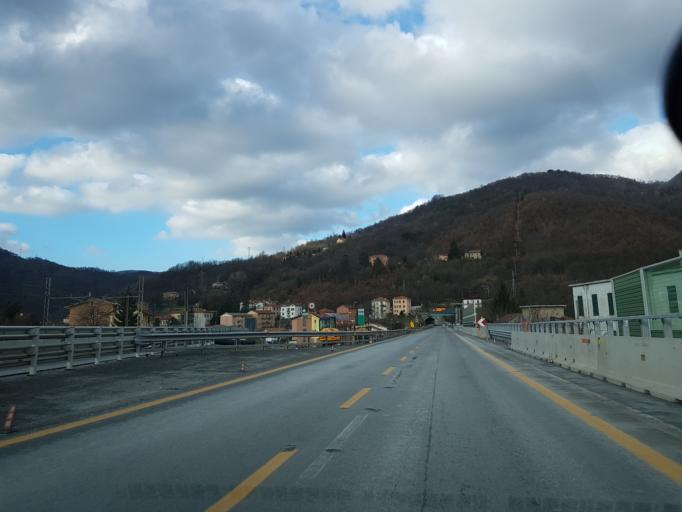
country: IT
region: Liguria
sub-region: Provincia di Genova
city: Ronco Scrivia
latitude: 44.6112
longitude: 8.9567
